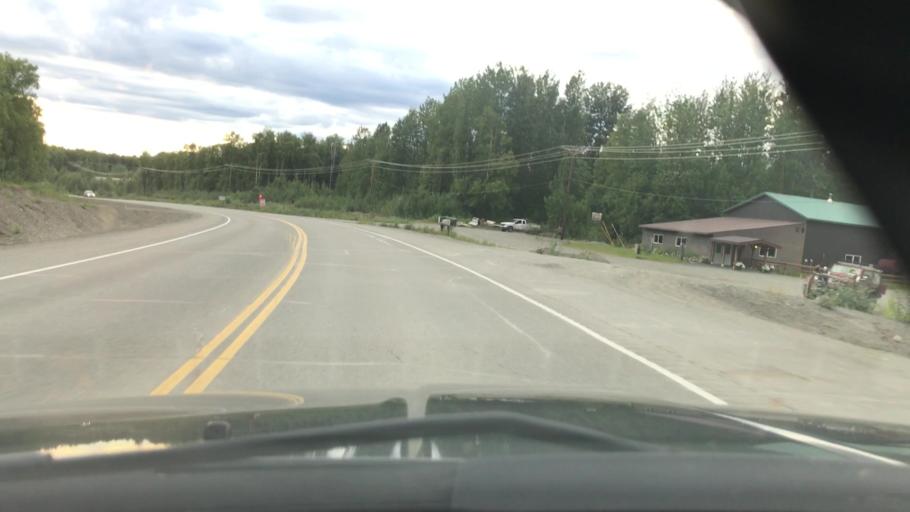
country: US
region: Alaska
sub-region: Matanuska-Susitna Borough
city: Y
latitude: 62.1381
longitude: -150.0452
